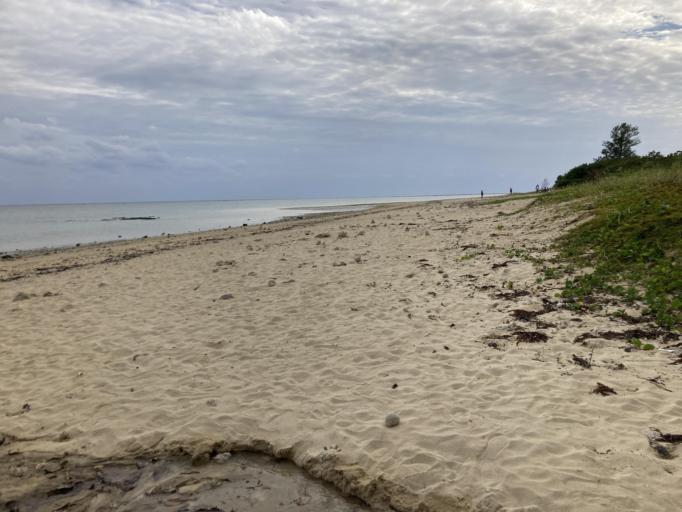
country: JP
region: Okinawa
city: Tomigusuku
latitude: 26.1398
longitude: 127.7965
